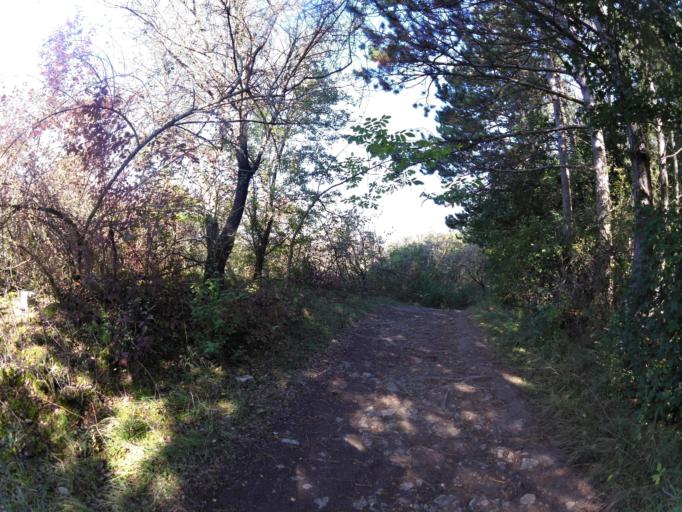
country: DE
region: Bavaria
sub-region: Regierungsbezirk Unterfranken
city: Sommerhausen
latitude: 49.6935
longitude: 10.0341
